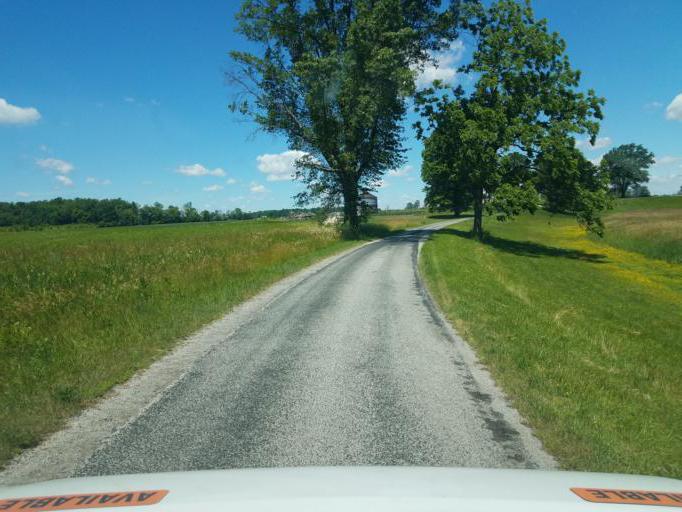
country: US
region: Ohio
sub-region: Crawford County
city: Bucyrus
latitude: 40.7300
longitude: -82.9225
